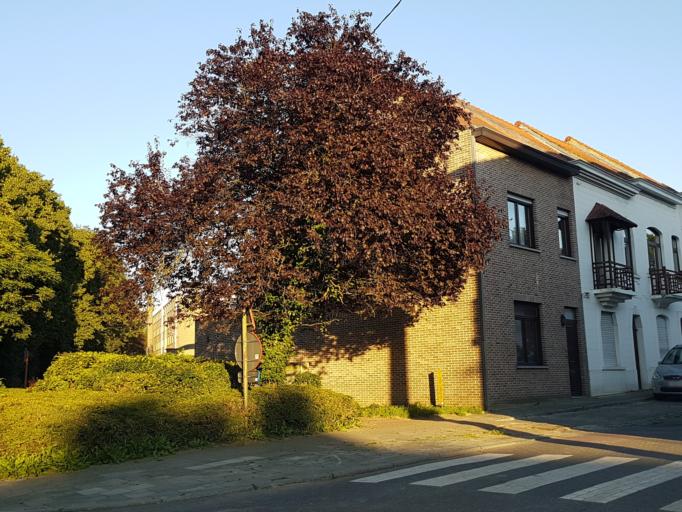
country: BE
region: Flanders
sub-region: Provincie Vlaams-Brabant
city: Dilbeek
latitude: 50.8675
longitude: 4.2445
